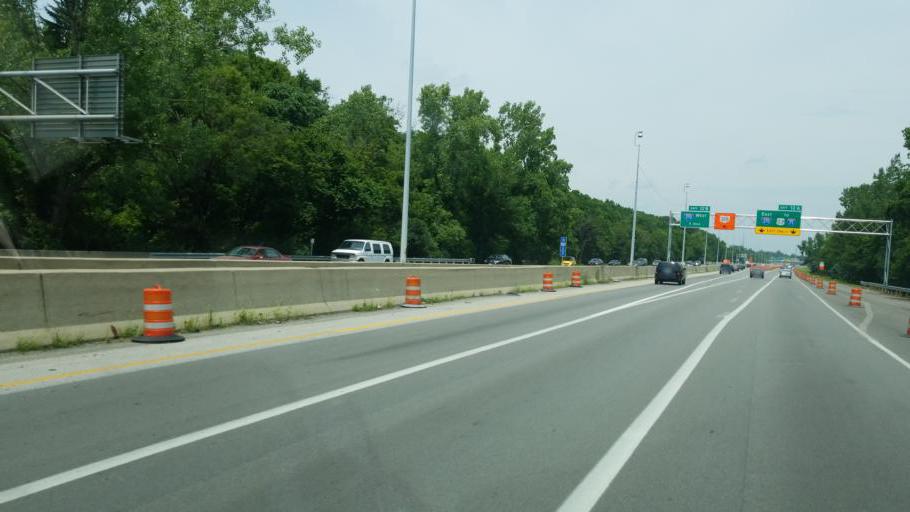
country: US
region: Ohio
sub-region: Franklin County
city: Worthington
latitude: 40.0972
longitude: -83.0365
